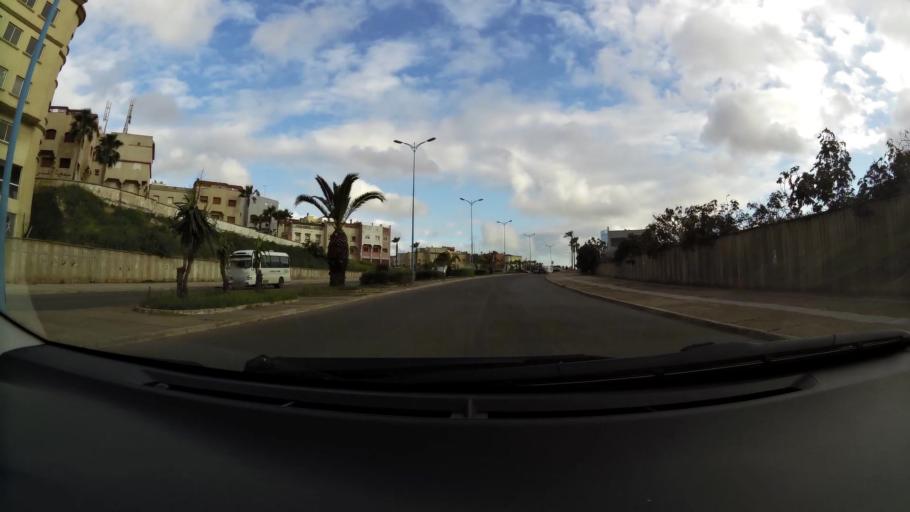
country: MA
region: Grand Casablanca
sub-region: Mohammedia
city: Mohammedia
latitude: 33.7013
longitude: -7.3708
